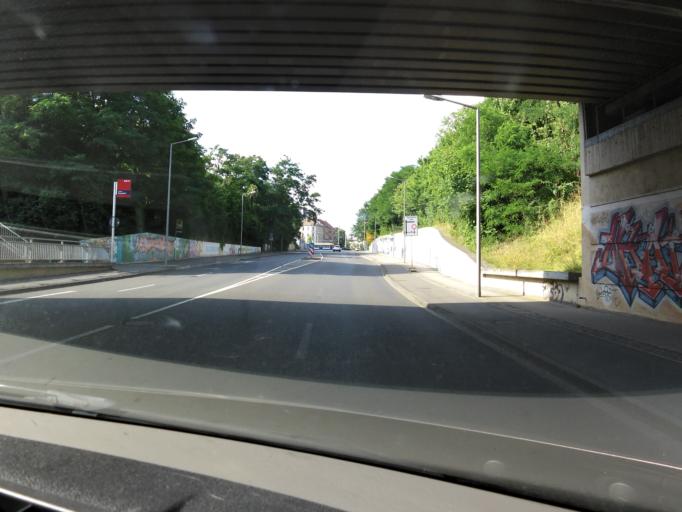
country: DE
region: Saxony
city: Taucha
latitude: 51.3442
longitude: 12.4452
